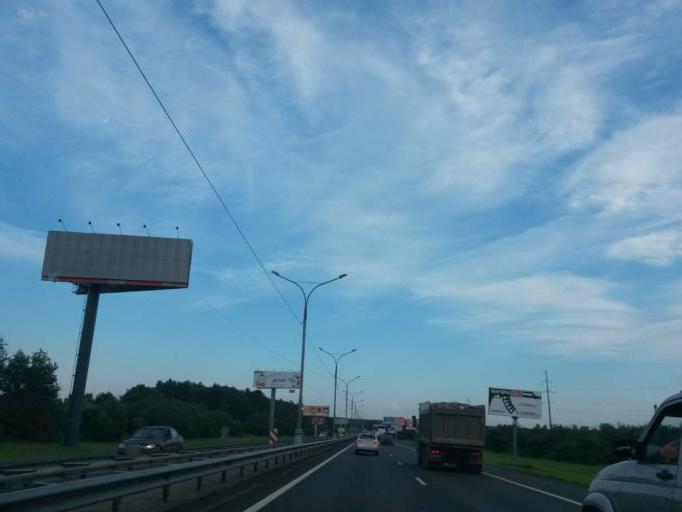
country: RU
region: Moskovskaya
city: Petrovskaya
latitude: 55.5678
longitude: 37.7676
